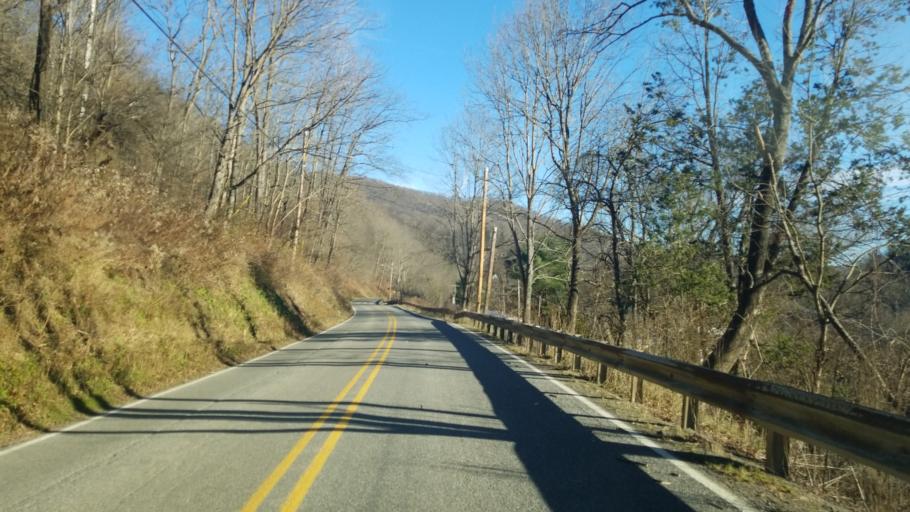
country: US
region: Pennsylvania
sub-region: Potter County
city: Coudersport
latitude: 41.6324
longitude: -78.0984
